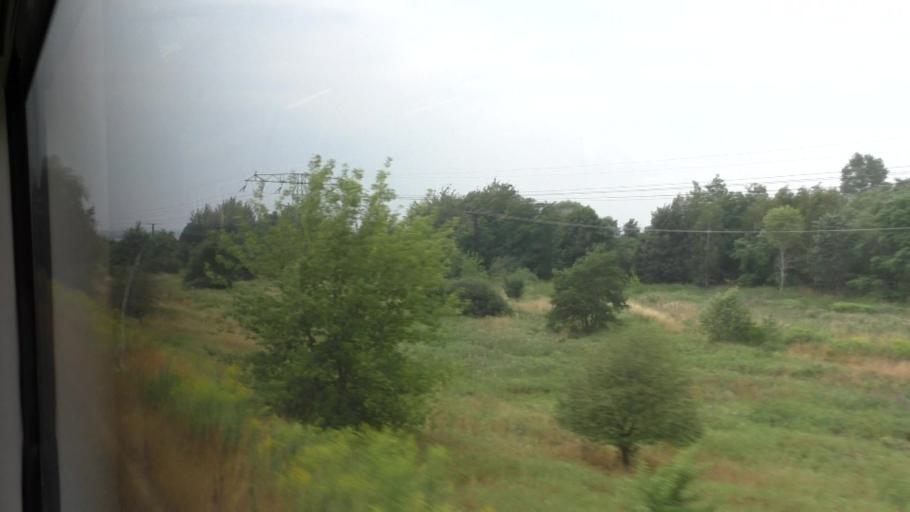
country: DE
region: Saxony
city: Goerlitz
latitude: 51.1092
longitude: 14.9766
